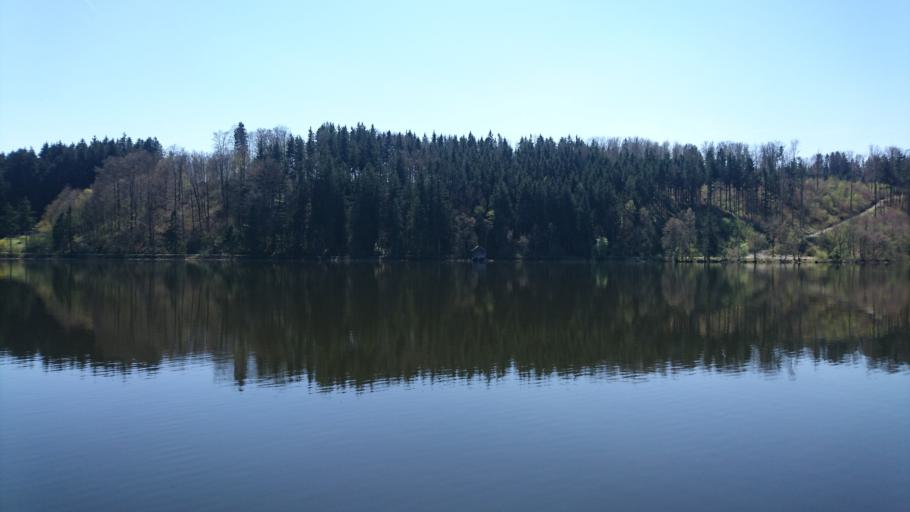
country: DE
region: Bavaria
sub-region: Upper Bavaria
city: Seehausen am Staffelsee
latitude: 47.6800
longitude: 11.1592
